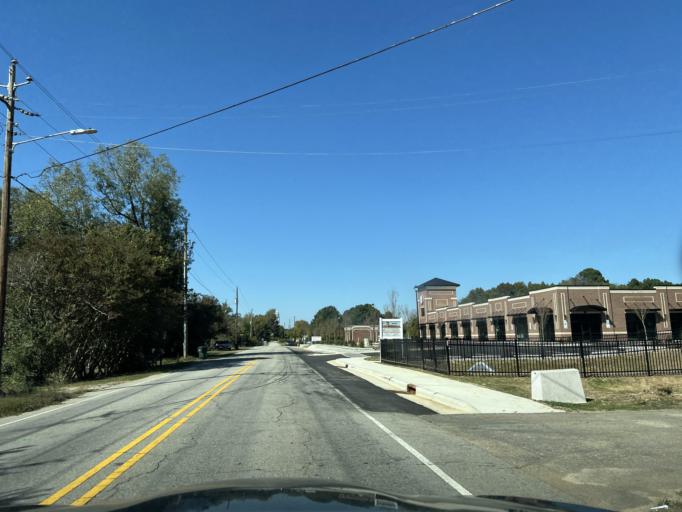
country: US
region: North Carolina
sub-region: Johnston County
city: Clayton
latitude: 35.6616
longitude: -78.4701
